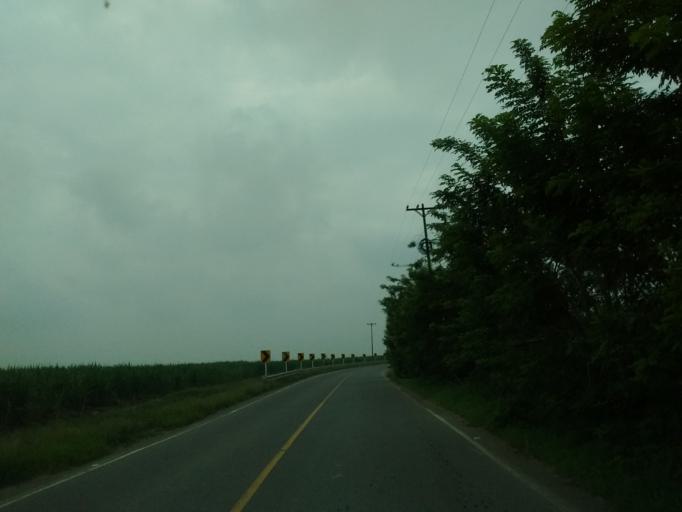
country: CO
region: Cauca
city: Puerto Tejada
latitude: 3.2222
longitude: -76.3724
